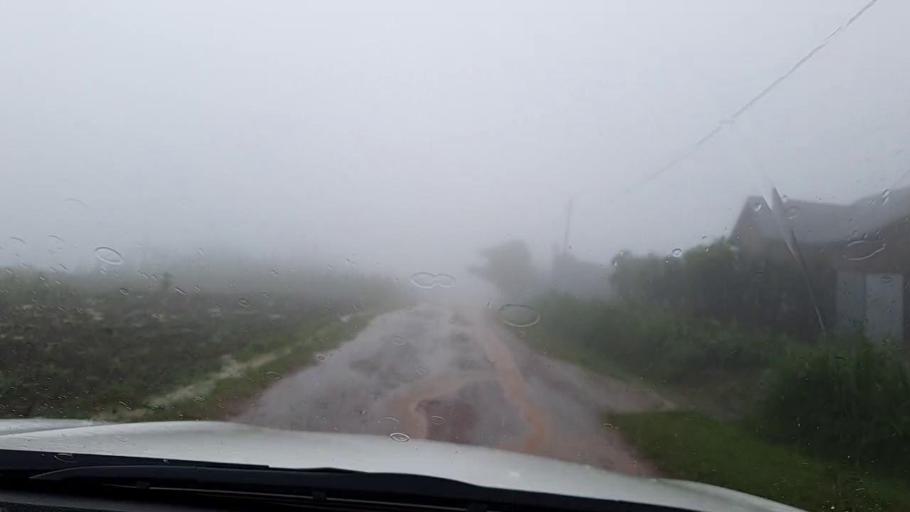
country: RW
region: Northern Province
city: Byumba
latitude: -1.7321
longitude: 30.0205
